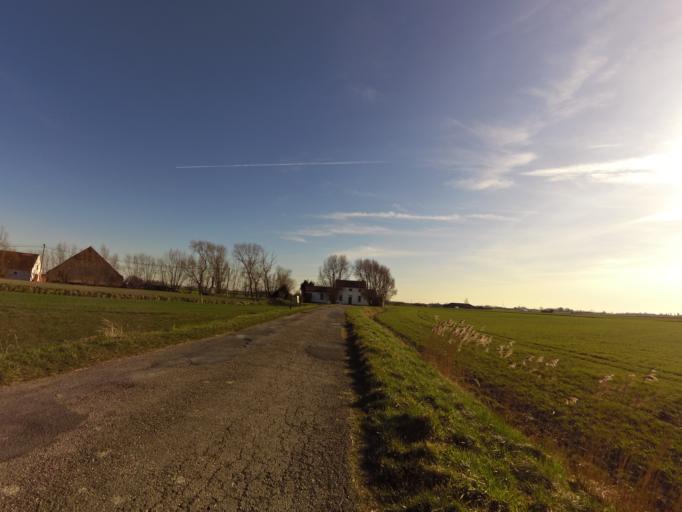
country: BE
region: Flanders
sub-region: Provincie West-Vlaanderen
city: Ostend
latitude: 51.1954
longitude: 2.9306
